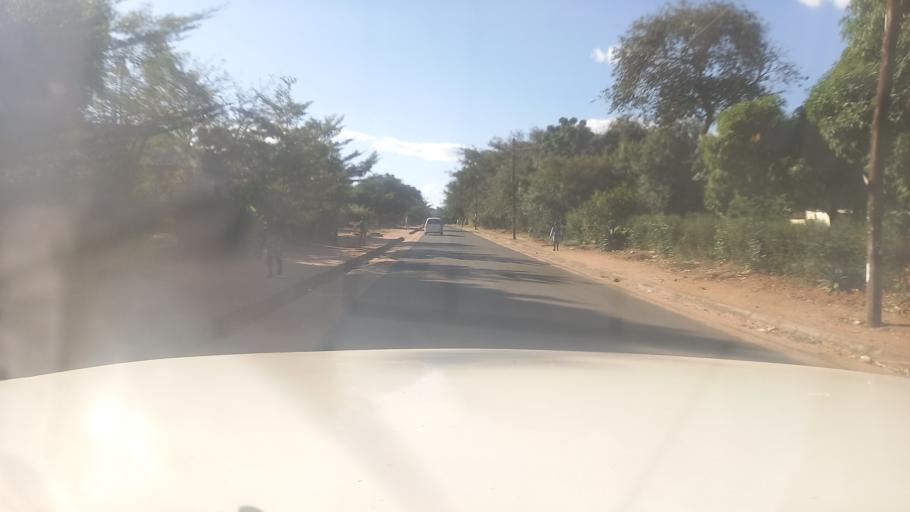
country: ZM
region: Southern
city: Livingstone
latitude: -17.8377
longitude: 25.8662
